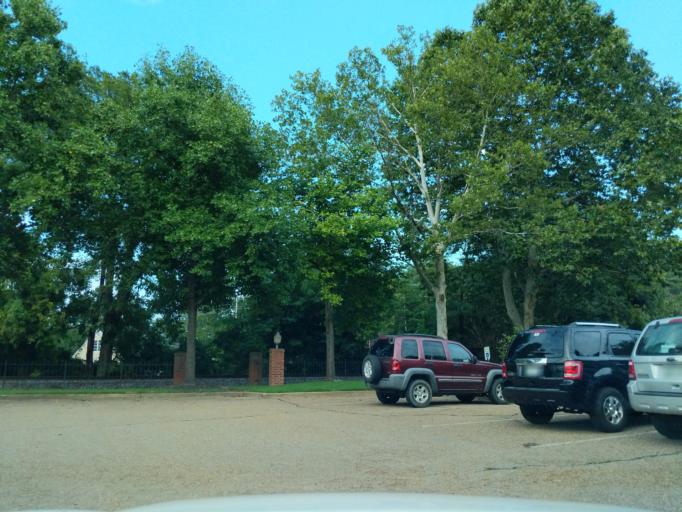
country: US
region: Tennessee
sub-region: Shelby County
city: Germantown
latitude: 35.0872
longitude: -89.8116
